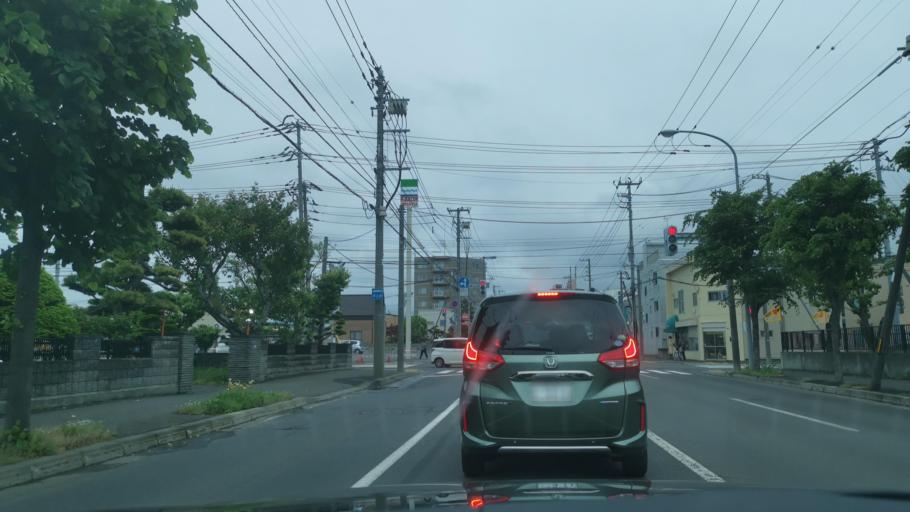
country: JP
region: Hokkaido
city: Sapporo
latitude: 43.1046
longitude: 141.3233
